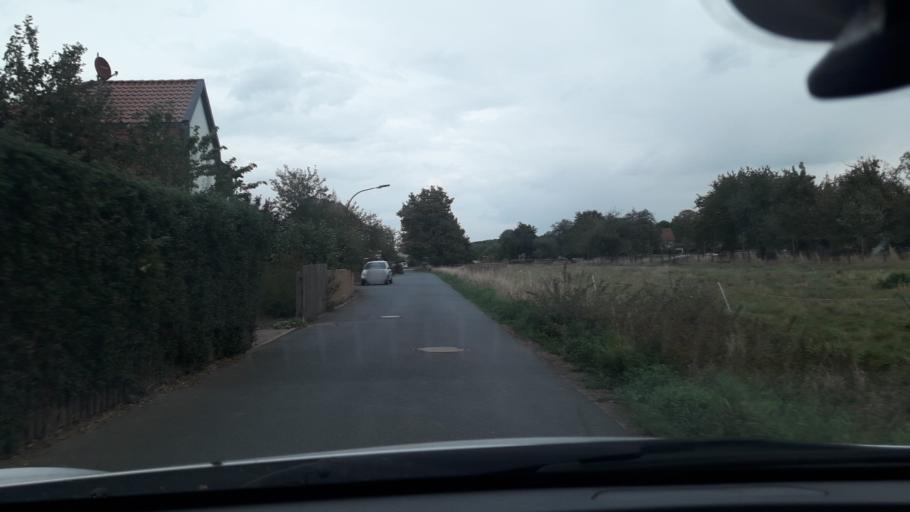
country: DE
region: Lower Saxony
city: Gielde
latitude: 52.0343
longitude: 10.4919
